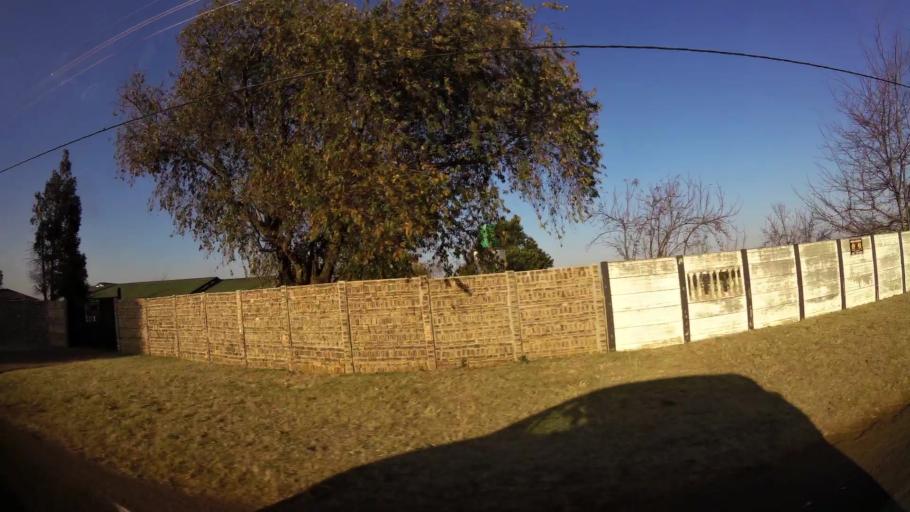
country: ZA
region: Gauteng
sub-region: West Rand District Municipality
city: Randfontein
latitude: -26.2082
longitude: 27.6438
